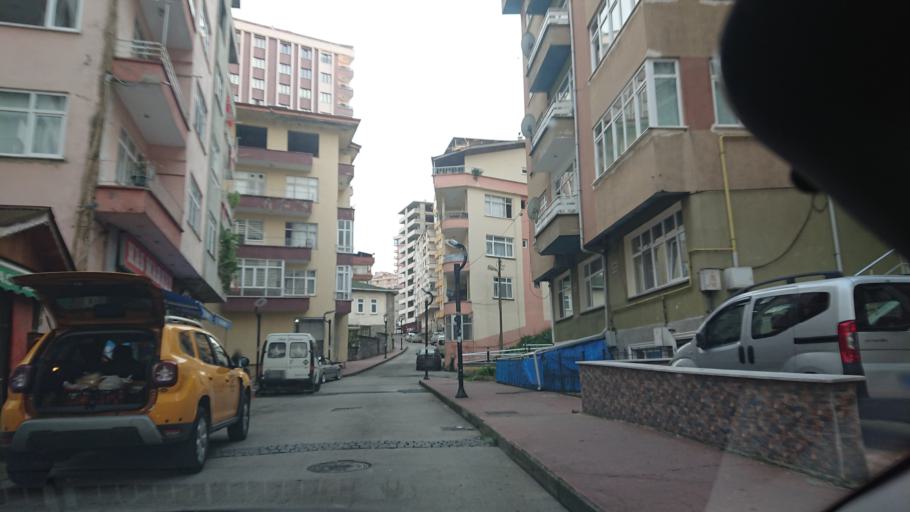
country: TR
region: Rize
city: Rize
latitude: 41.0219
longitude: 40.5162
